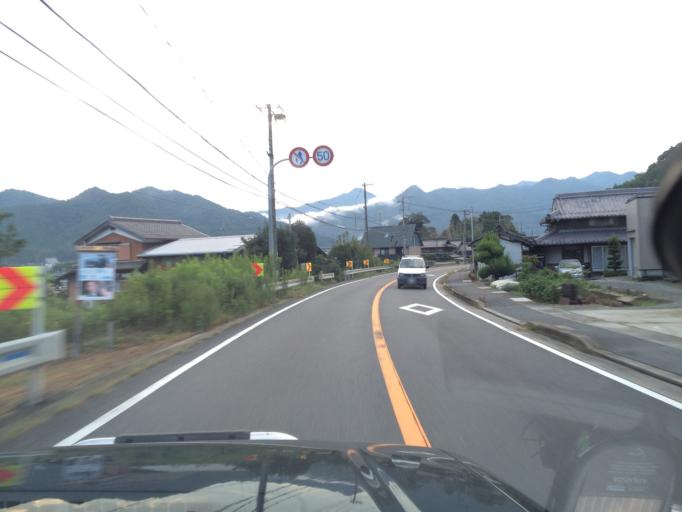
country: JP
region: Hyogo
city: Nishiwaki
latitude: 35.0923
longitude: 134.9986
